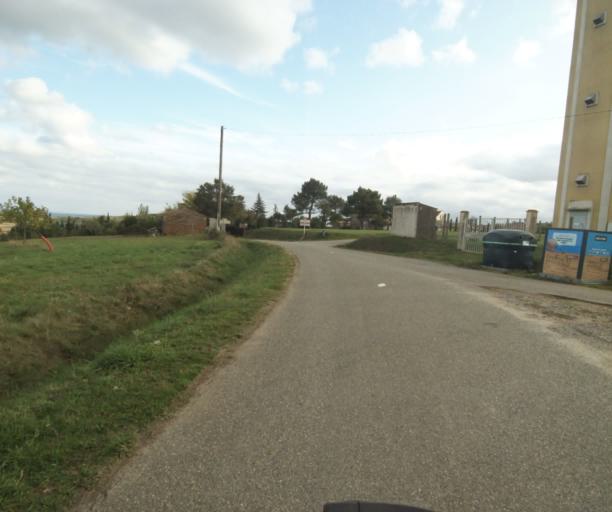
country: FR
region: Midi-Pyrenees
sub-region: Departement de la Haute-Garonne
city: Launac
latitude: 43.8234
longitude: 1.1170
